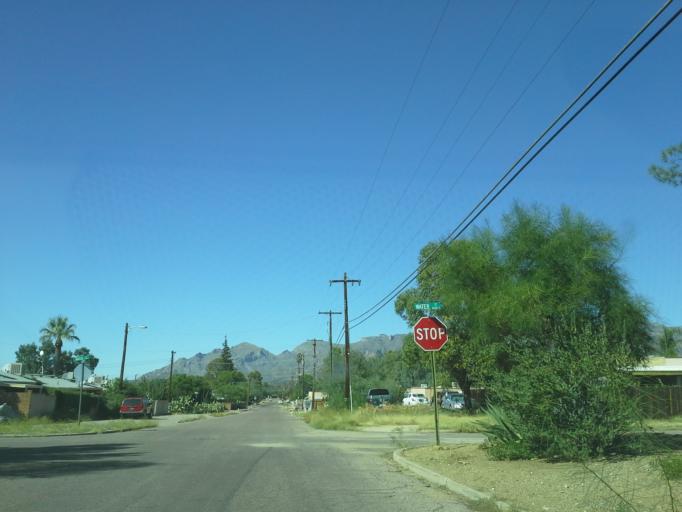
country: US
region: Arizona
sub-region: Pima County
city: Tucson
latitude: 32.2519
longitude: -110.9332
